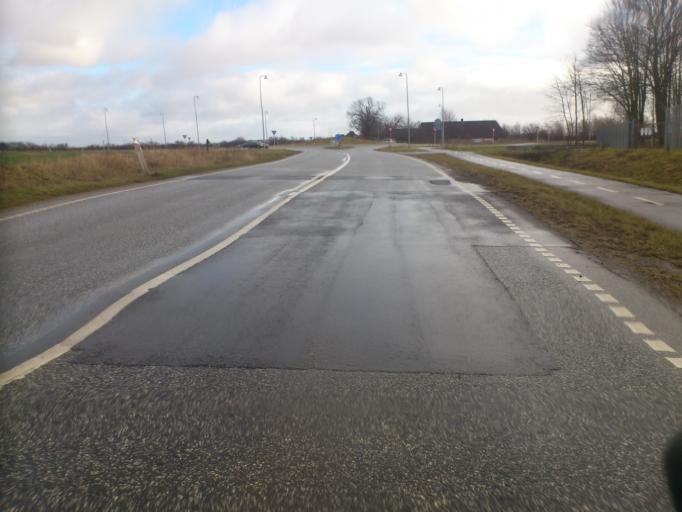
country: DK
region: South Denmark
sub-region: Fredericia Kommune
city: Fredericia
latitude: 55.6003
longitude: 9.7564
